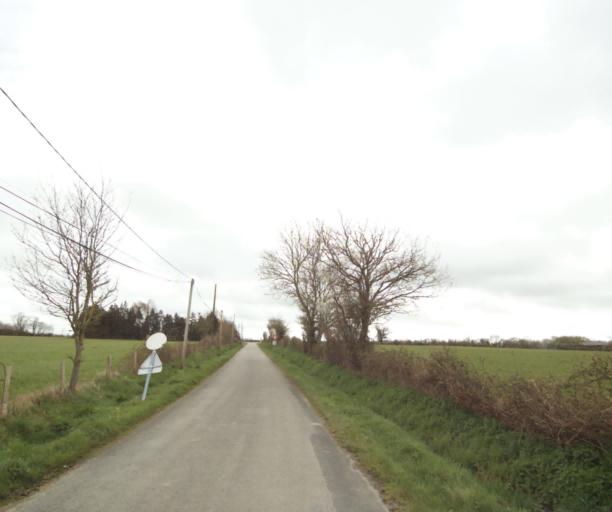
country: FR
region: Pays de la Loire
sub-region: Departement de la Loire-Atlantique
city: Bouvron
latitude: 47.4293
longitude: -1.8560
